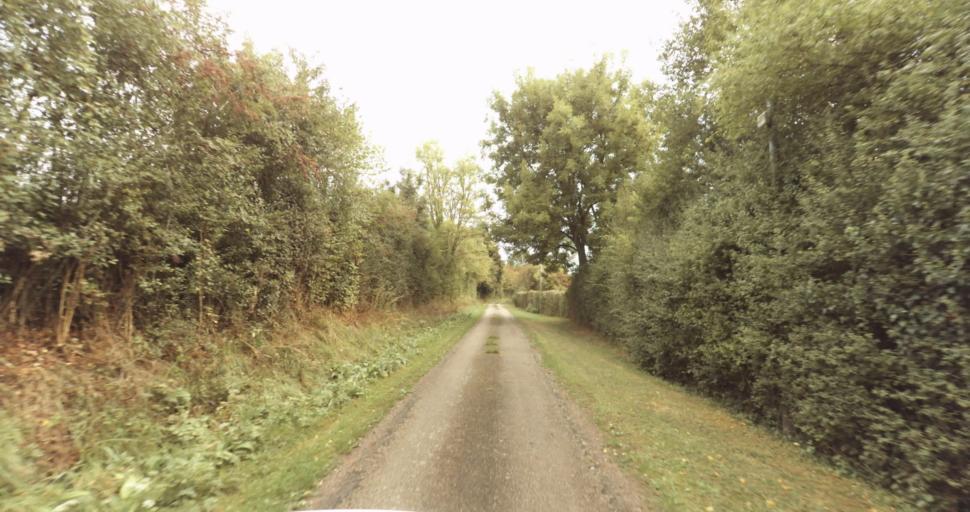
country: FR
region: Lower Normandy
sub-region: Departement du Calvados
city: Livarot
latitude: 48.9306
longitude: 0.0944
